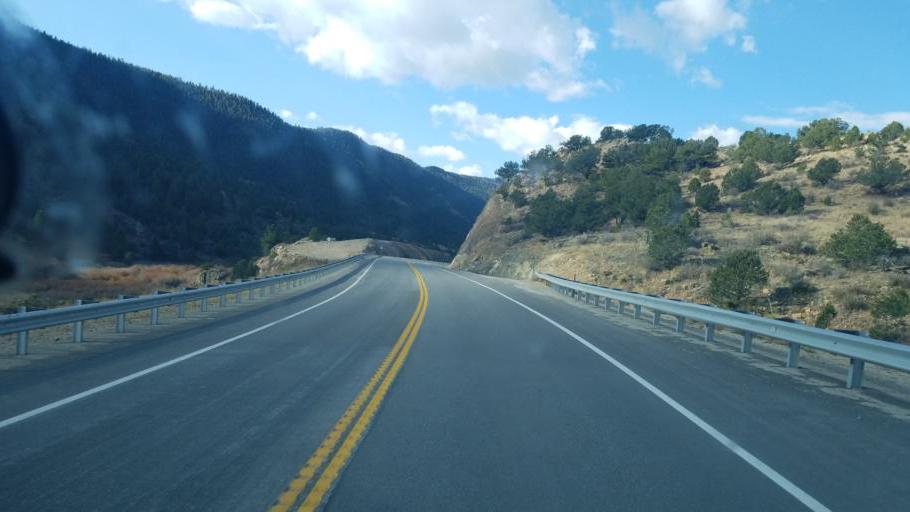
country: US
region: Colorado
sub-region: Chaffee County
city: Buena Vista
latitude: 38.8345
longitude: -106.0233
